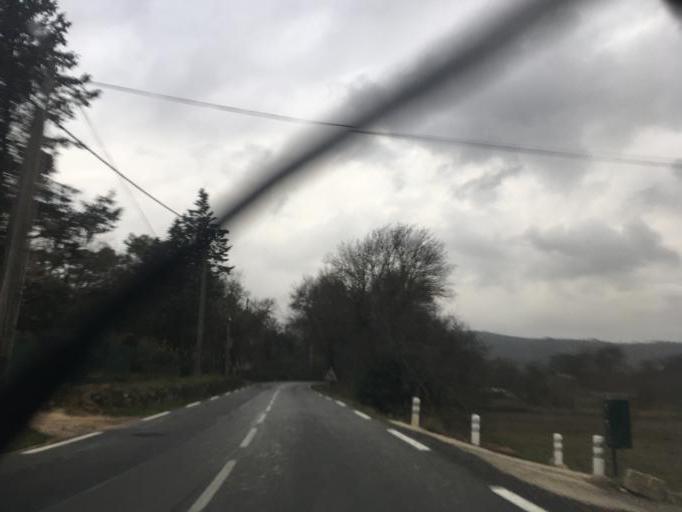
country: FR
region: Provence-Alpes-Cote d'Azur
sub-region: Departement du Var
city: Forcalqueiret
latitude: 43.3404
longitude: 6.0959
